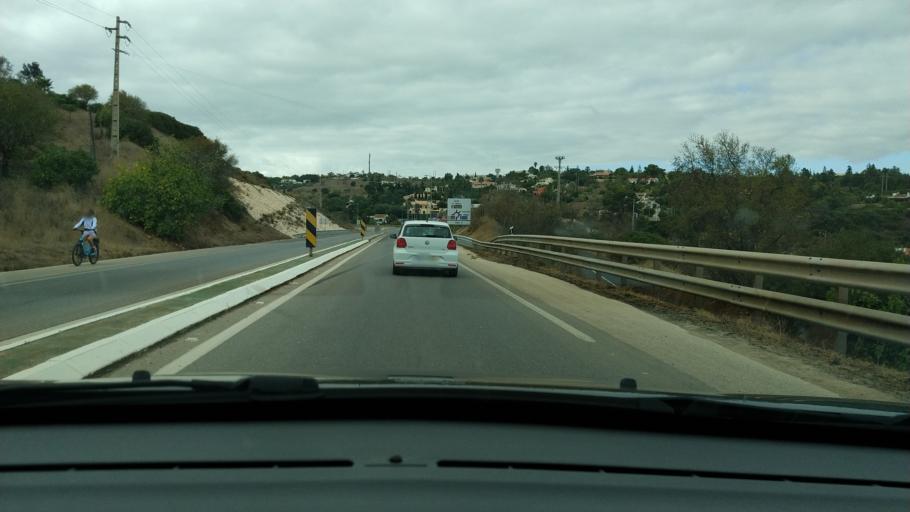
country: PT
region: Faro
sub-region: Lagos
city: Lagos
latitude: 37.1052
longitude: -8.7043
